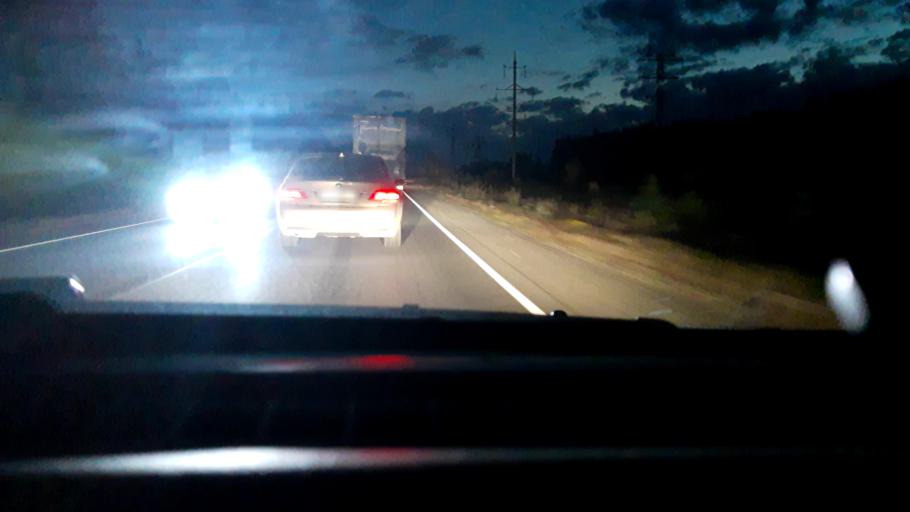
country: RU
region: Nizjnij Novgorod
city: Lukino
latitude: 56.3921
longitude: 43.6434
